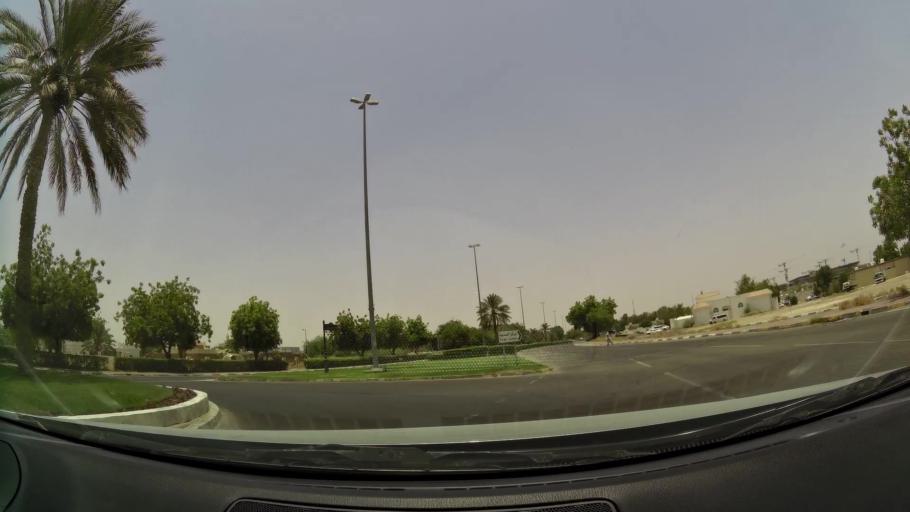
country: AE
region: Abu Dhabi
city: Al Ain
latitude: 24.2215
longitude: 55.7326
